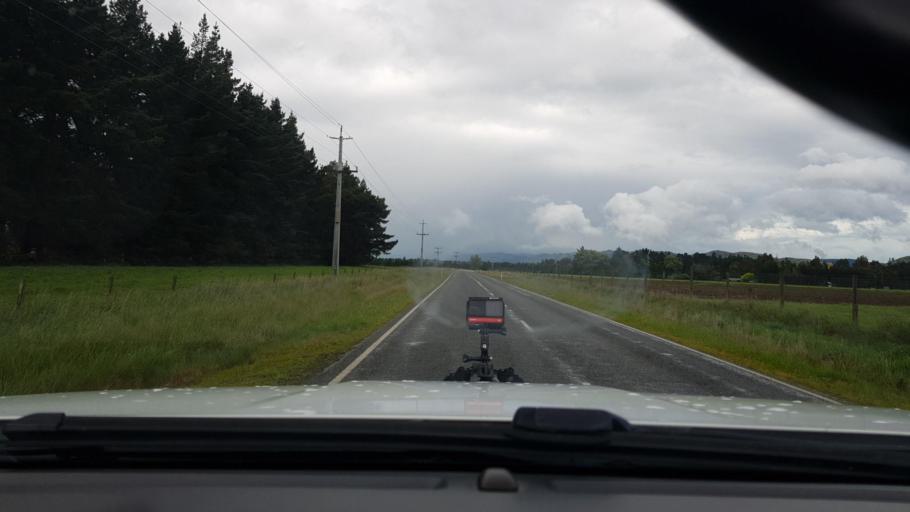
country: NZ
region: Southland
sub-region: Southland District
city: Winton
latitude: -45.7590
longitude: 168.4077
